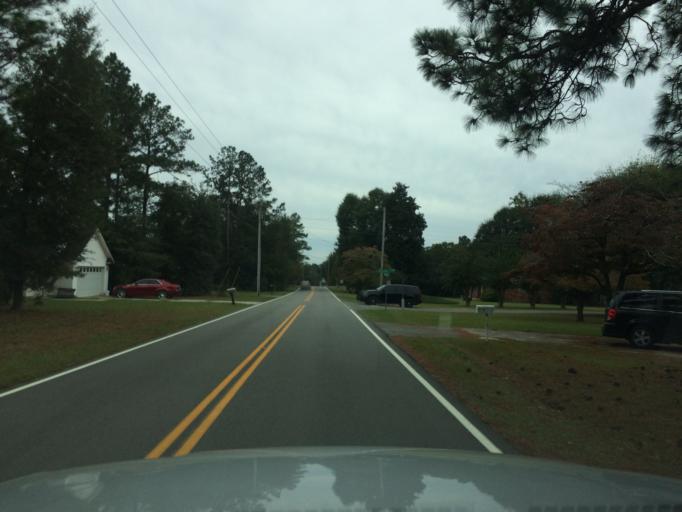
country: US
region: South Carolina
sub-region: Aiken County
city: New Ellenton
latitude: 33.4267
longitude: -81.6887
